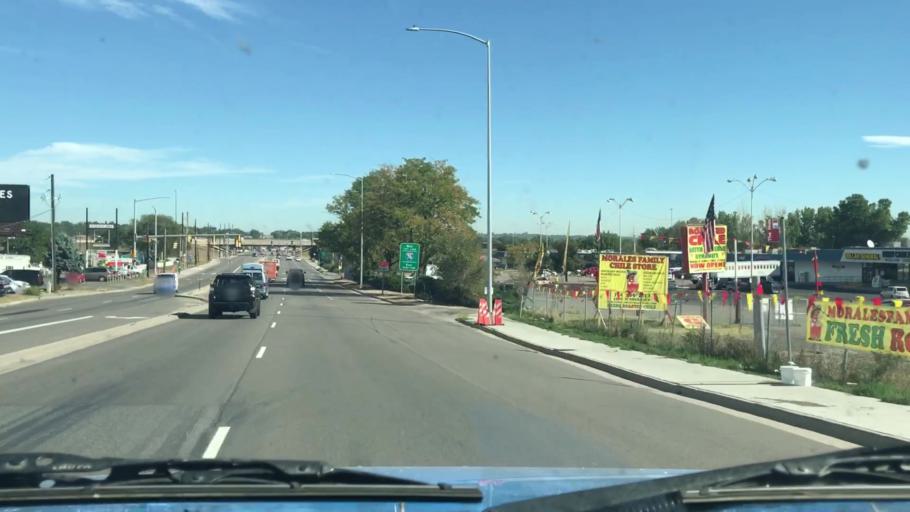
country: US
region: Colorado
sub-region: Adams County
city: Berkley
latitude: 39.7914
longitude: -105.0532
